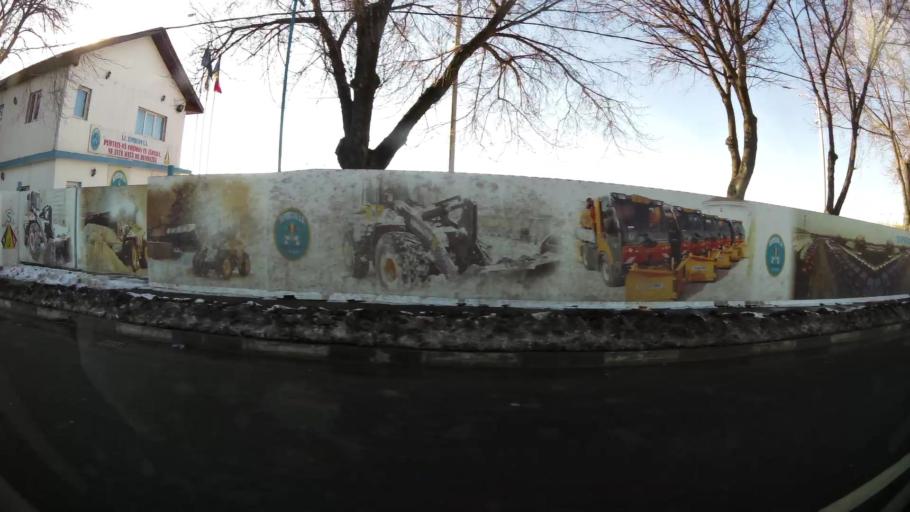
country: RO
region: Ilfov
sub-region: Comuna Fundeni-Dobroesti
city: Fundeni
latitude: 44.4738
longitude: 26.1411
